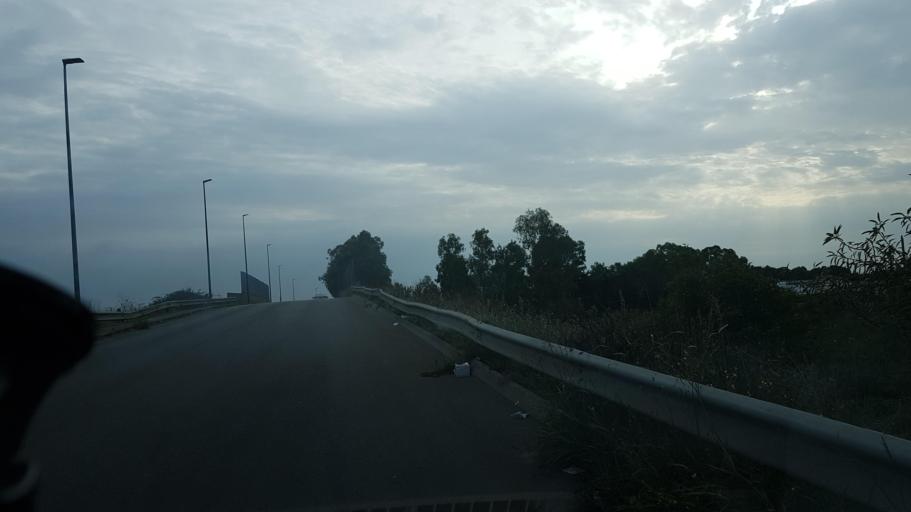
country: IT
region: Apulia
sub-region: Provincia di Lecce
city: Trepuzzi
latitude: 40.4135
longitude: 18.0741
